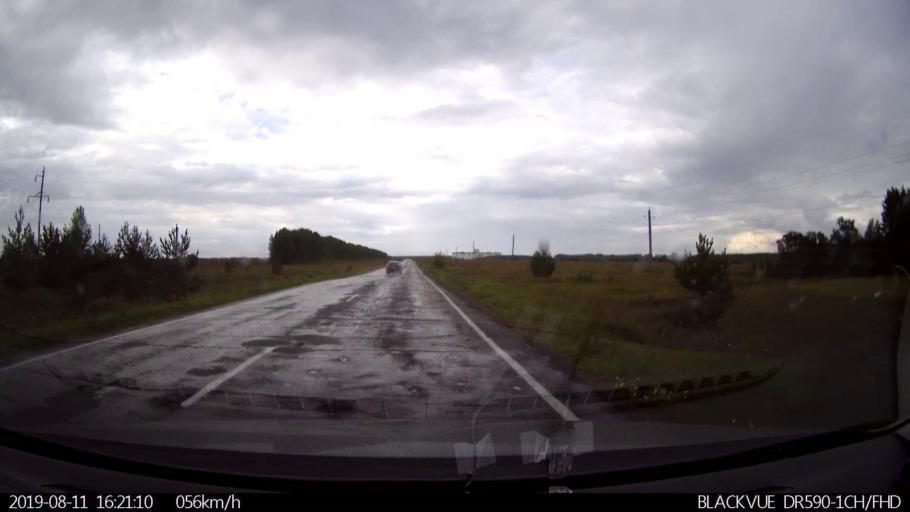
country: RU
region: Ulyanovsk
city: Mayna
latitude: 54.0777
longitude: 47.5993
